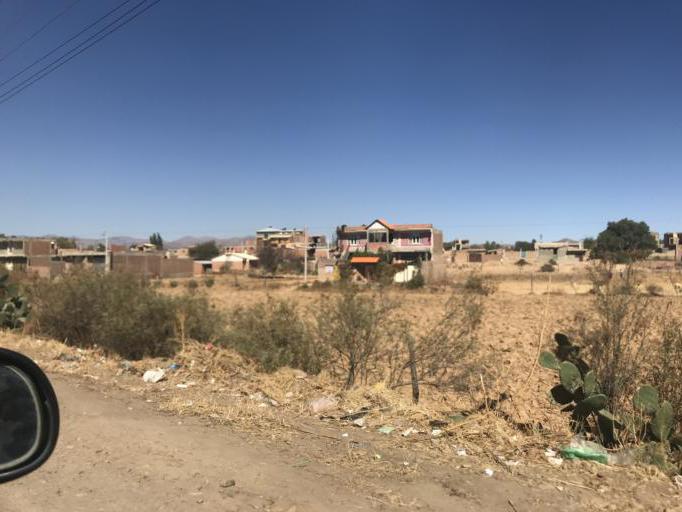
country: BO
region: Cochabamba
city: Cliza
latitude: -17.5937
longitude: -65.9399
